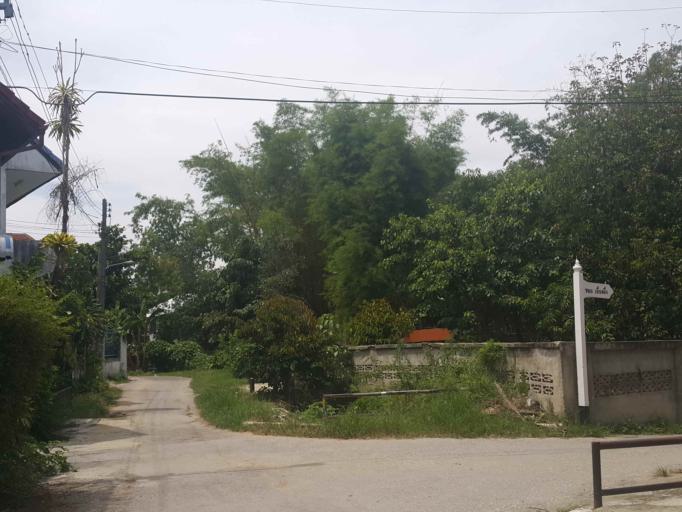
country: TH
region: Chiang Mai
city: Chiang Mai
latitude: 18.7630
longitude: 99.0125
